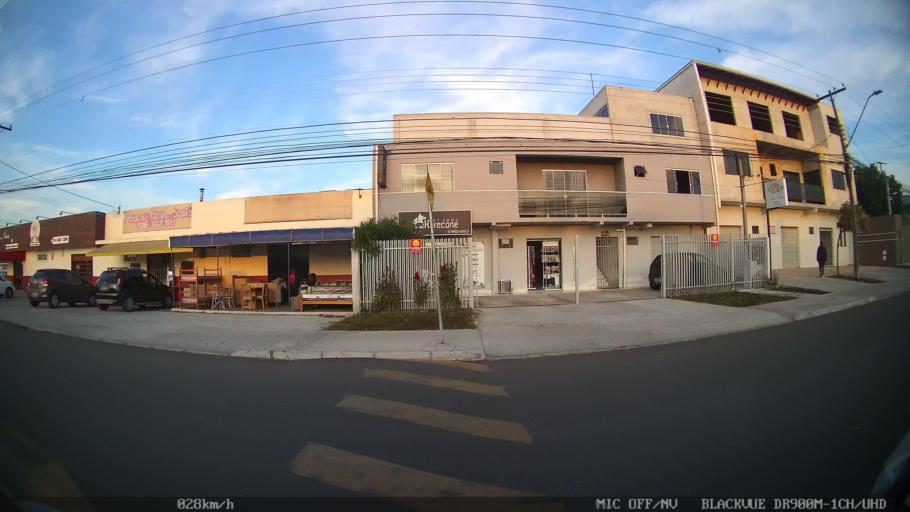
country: BR
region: Parana
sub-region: Pinhais
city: Pinhais
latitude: -25.4617
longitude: -49.1858
